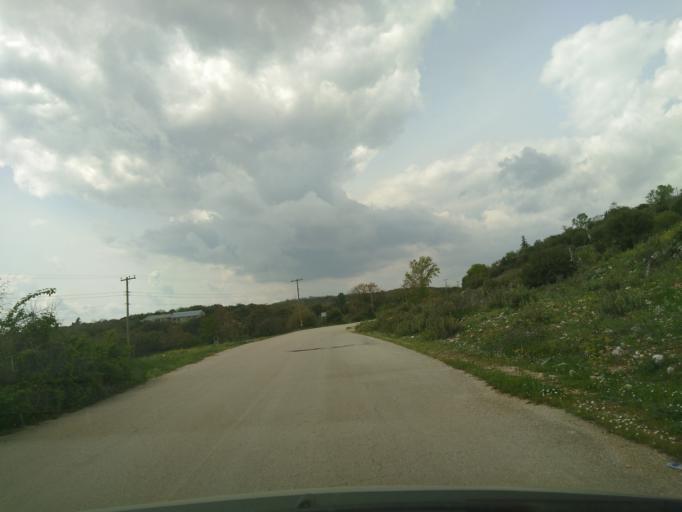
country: GR
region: Epirus
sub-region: Nomos Ioanninon
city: Asprangeloi
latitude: 39.7750
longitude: 20.6897
